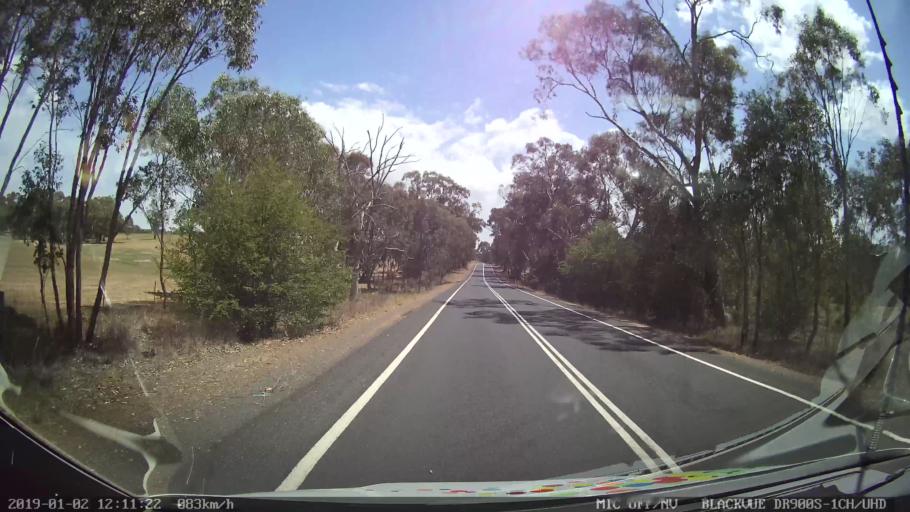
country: AU
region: New South Wales
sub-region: Young
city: Young
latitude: -34.4499
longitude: 148.2573
